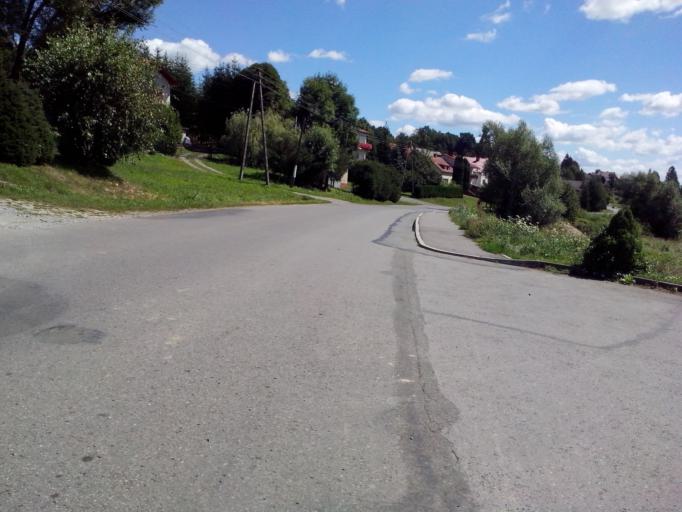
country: PL
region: Subcarpathian Voivodeship
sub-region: Powiat brzozowski
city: Domaradz
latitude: 49.7925
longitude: 21.9596
